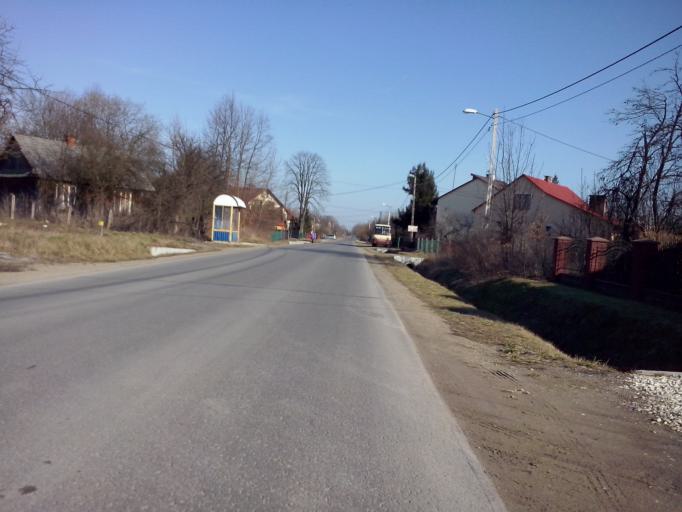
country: PL
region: Subcarpathian Voivodeship
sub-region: Powiat nizanski
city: Krzeszow
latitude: 50.4155
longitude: 22.3592
